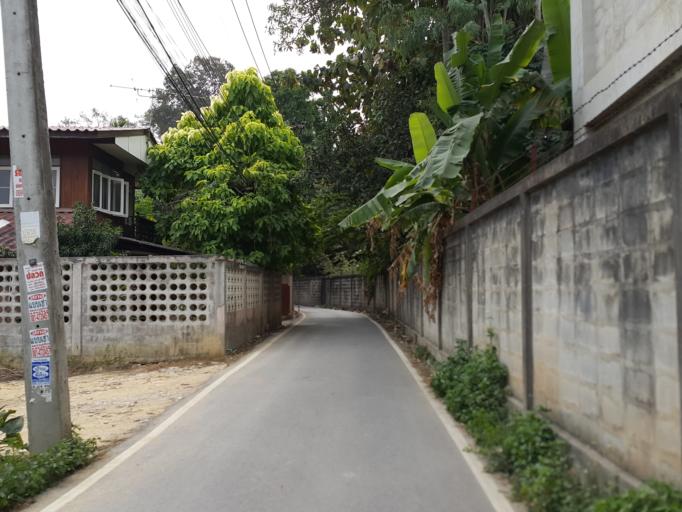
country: TH
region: Chiang Mai
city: Saraphi
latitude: 18.7327
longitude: 99.0213
